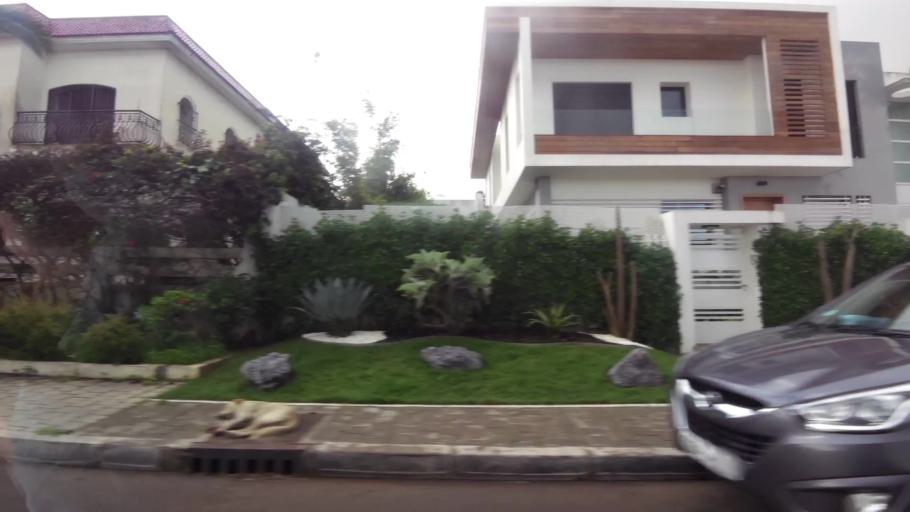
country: MA
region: Grand Casablanca
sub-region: Casablanca
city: Casablanca
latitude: 33.5477
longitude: -7.6584
